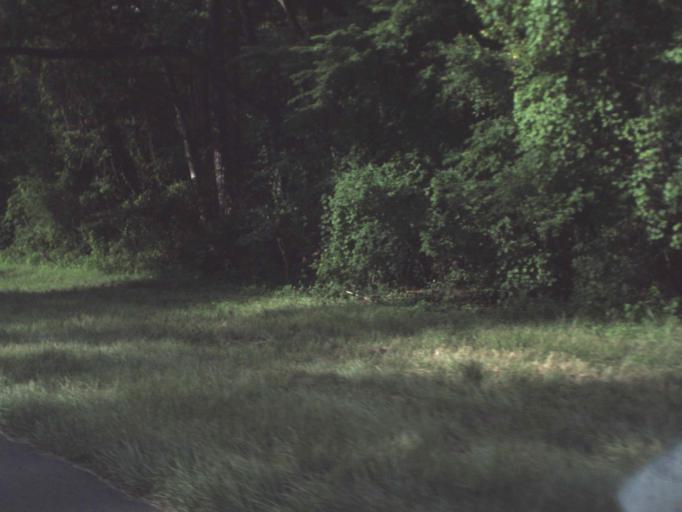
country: US
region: Florida
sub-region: Hernando County
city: North Brooksville
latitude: 28.6282
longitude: -82.4223
